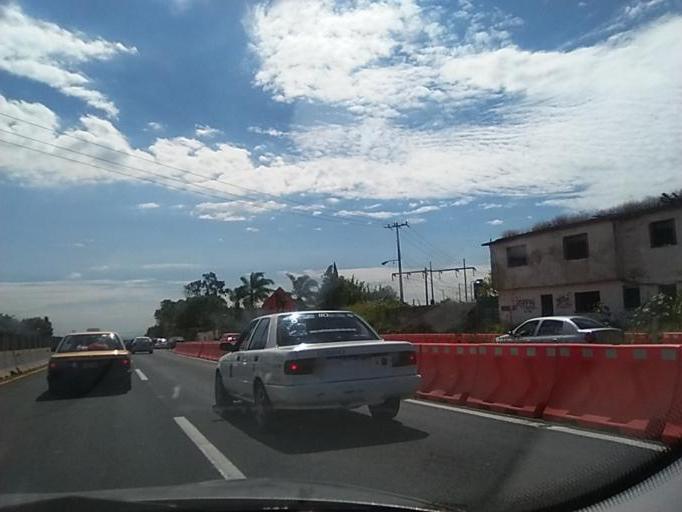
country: MX
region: Morelos
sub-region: Cuernavaca
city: Fraccionamiento Lomas de Ahuatlan
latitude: 18.9598
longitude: -99.2277
